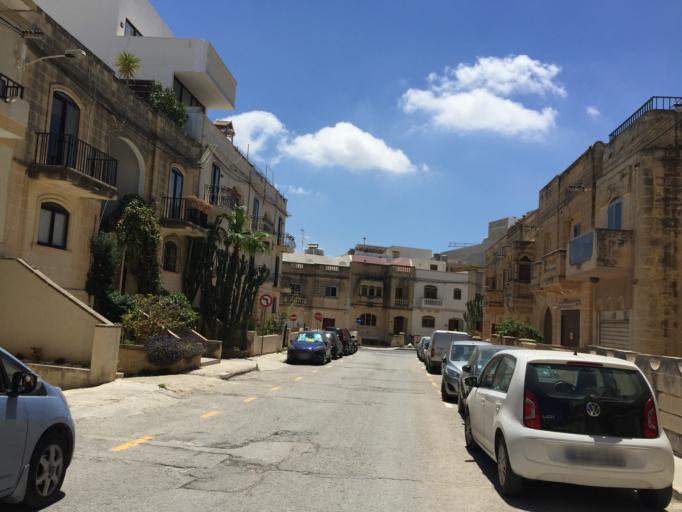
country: MT
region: Is-Swieqi
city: Swieqi
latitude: 35.9207
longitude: 14.4824
